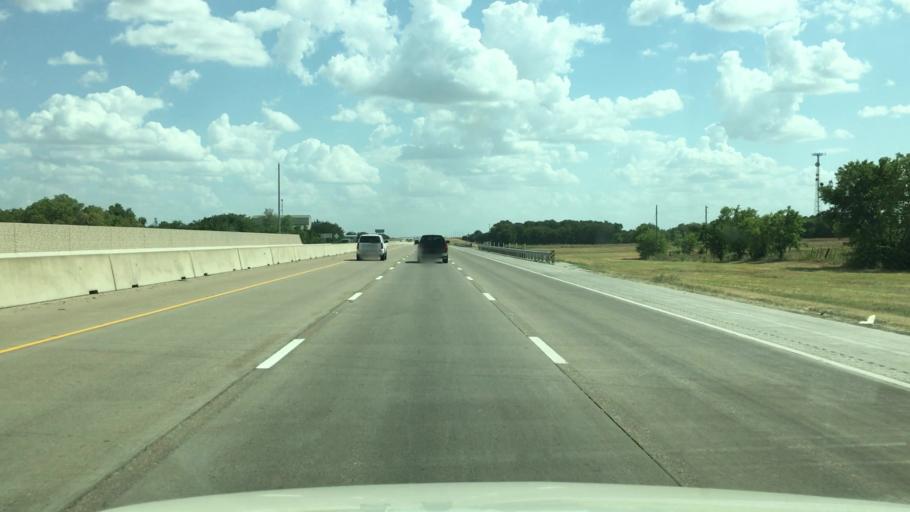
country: US
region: Texas
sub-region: Ellis County
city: Waxahachie
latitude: 32.3389
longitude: -96.8566
